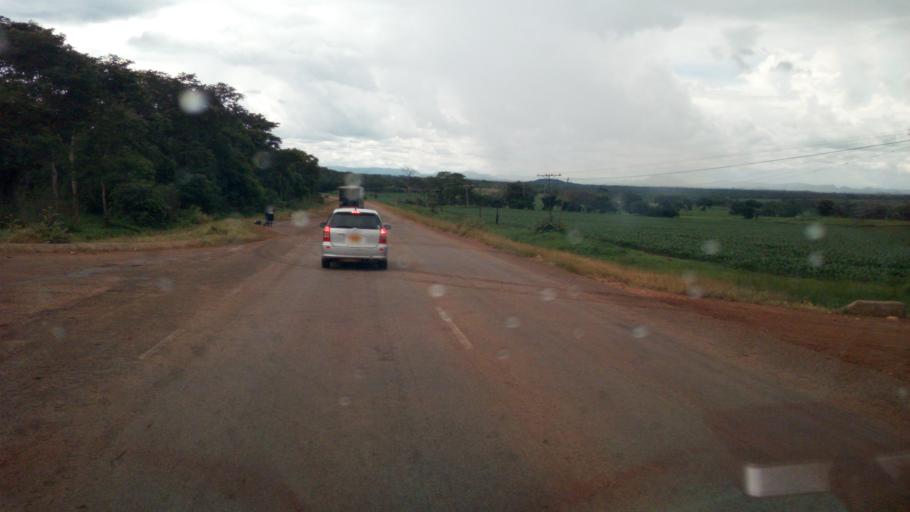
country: ZW
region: Mashonaland Central
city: Glendale
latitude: -17.3303
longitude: 31.1490
